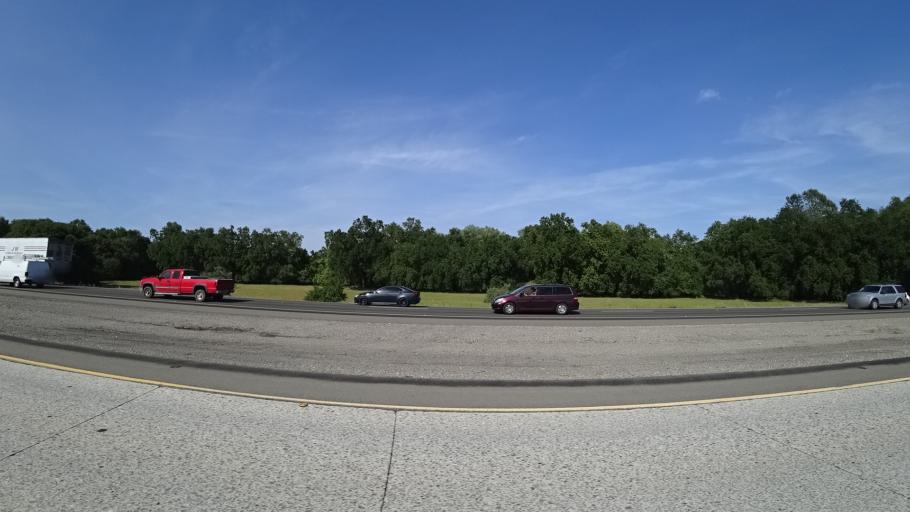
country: US
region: California
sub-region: Butte County
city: Durham
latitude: 39.6923
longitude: -121.7761
